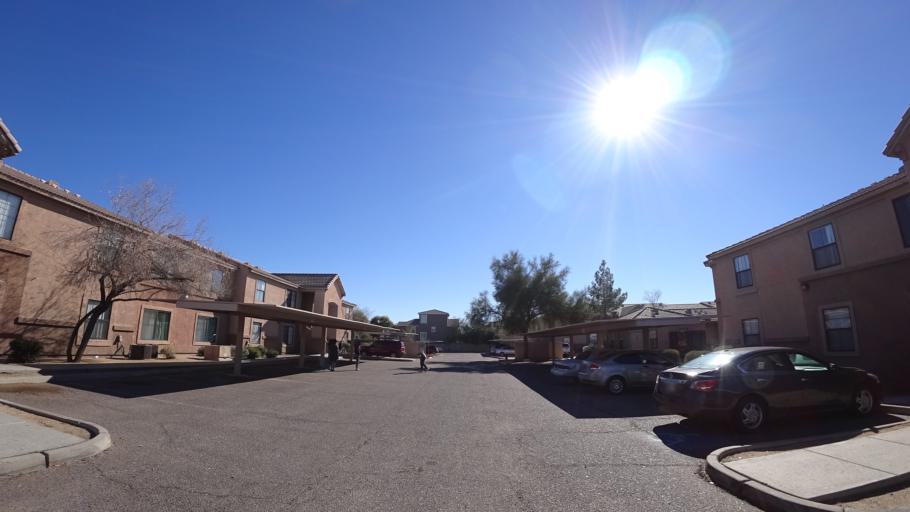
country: US
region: Arizona
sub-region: Maricopa County
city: Avondale
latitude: 33.4332
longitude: -112.3368
